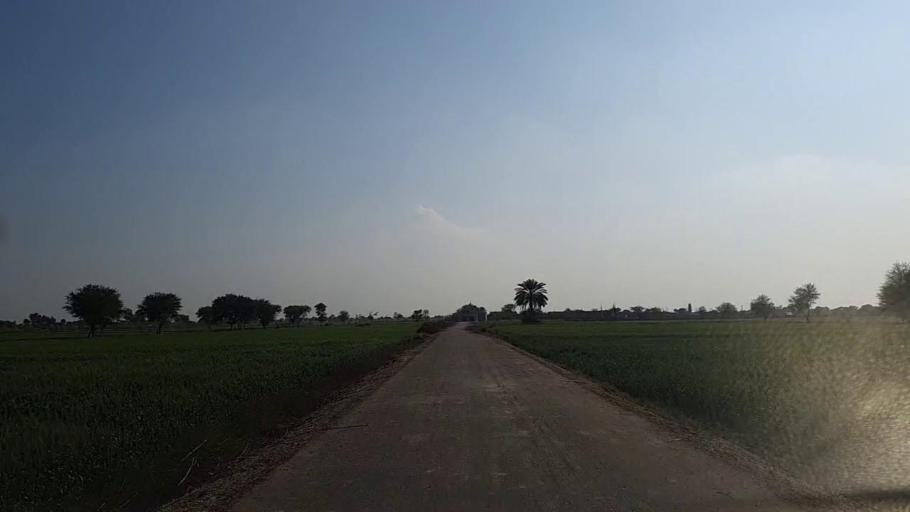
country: PK
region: Sindh
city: Jam Sahib
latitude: 26.2817
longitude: 68.6136
